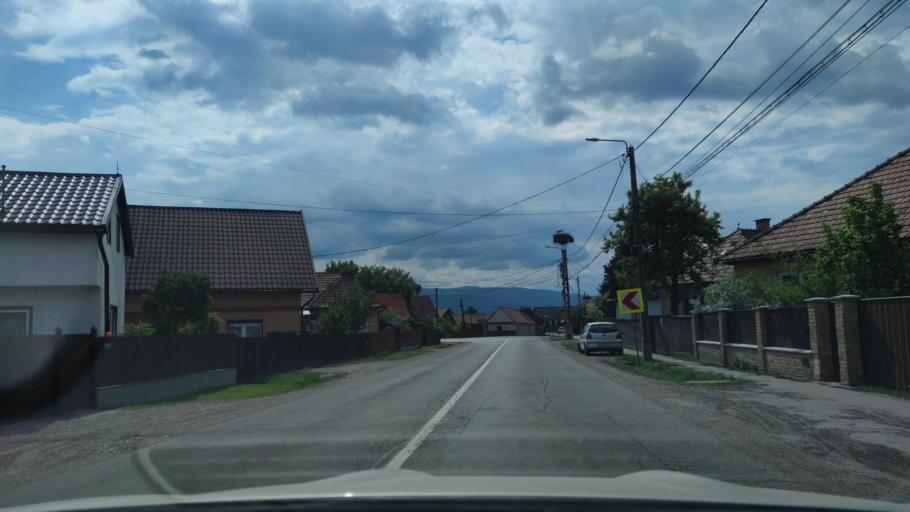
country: RO
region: Harghita
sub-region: Comuna Joseni
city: Joseni
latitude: 46.7036
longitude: 25.4937
